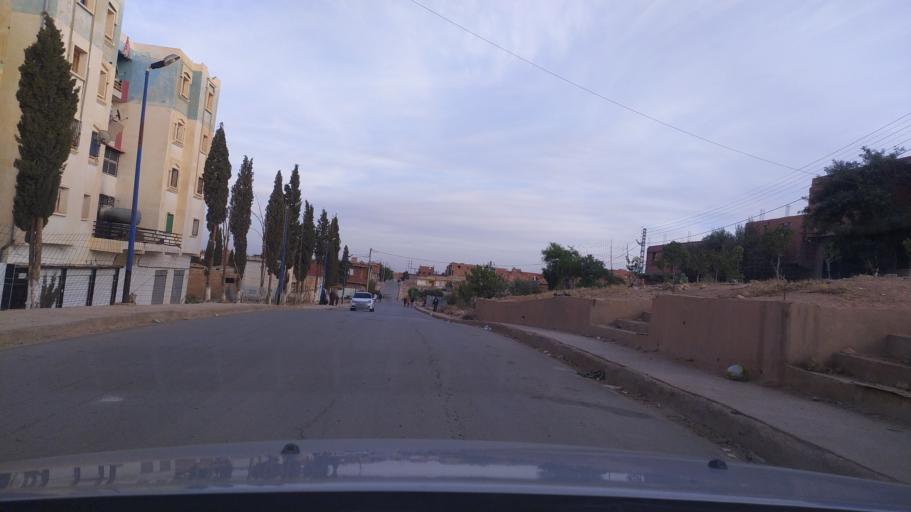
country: DZ
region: Tiaret
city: Frenda
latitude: 34.8943
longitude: 1.2400
